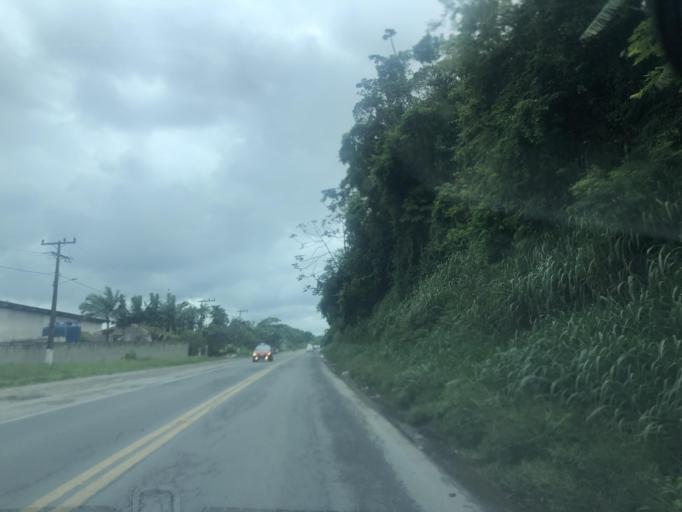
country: BR
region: Santa Catarina
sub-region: Sao Francisco Do Sul
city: Sao Francisco do Sul
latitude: -26.2415
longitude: -48.6174
